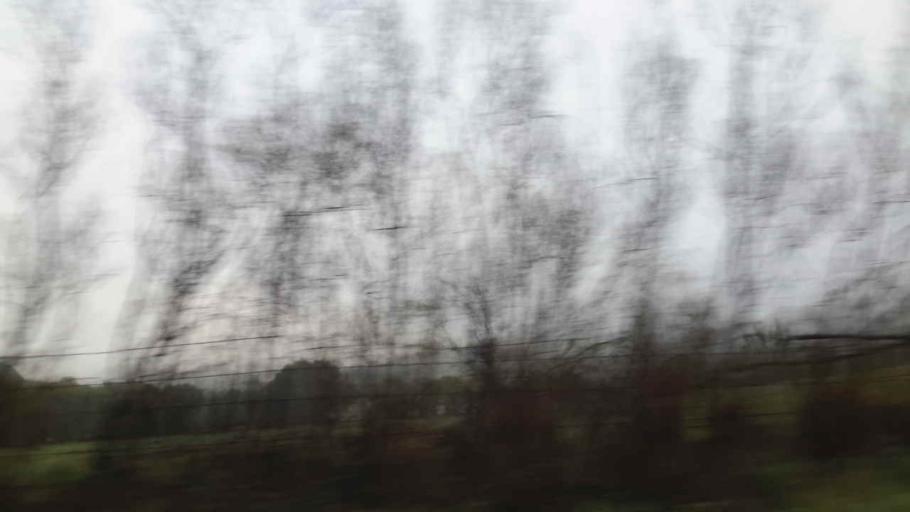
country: AU
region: New South Wales
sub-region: Wollondilly
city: Douglas Park
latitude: -34.1694
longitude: 150.7136
